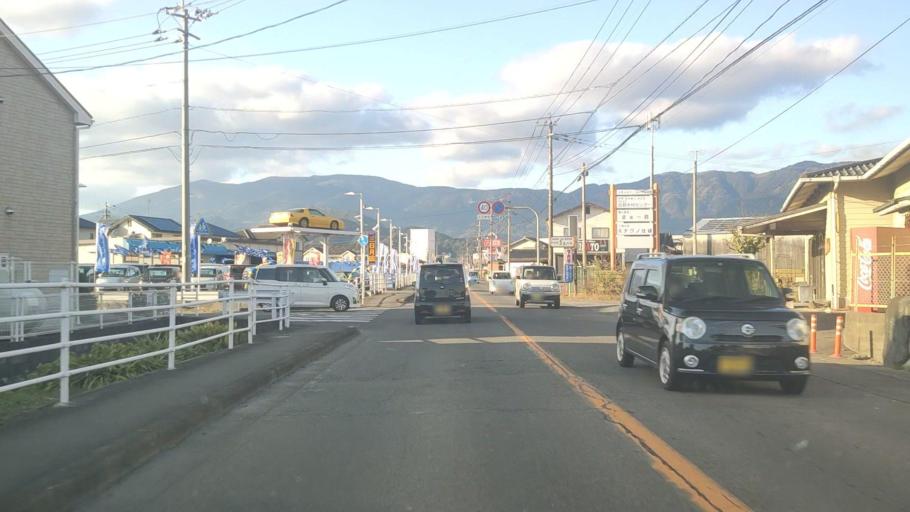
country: JP
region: Saga Prefecture
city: Saga-shi
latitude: 33.2850
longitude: 130.2089
